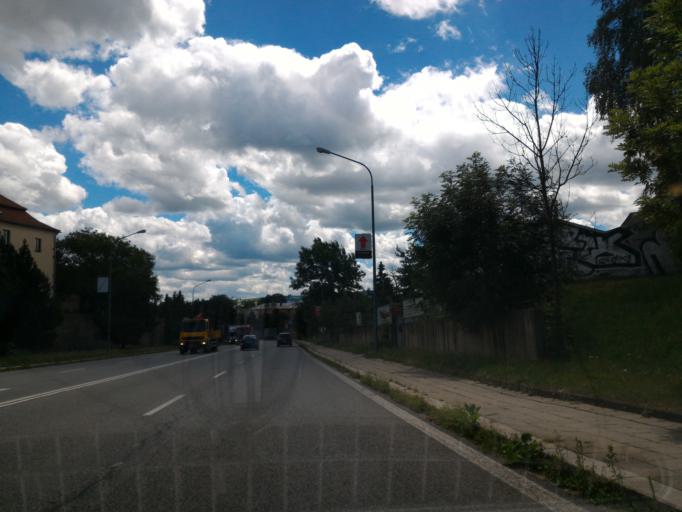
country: CZ
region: Vysocina
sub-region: Okres Jihlava
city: Jihlava
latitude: 49.3945
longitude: 15.5863
